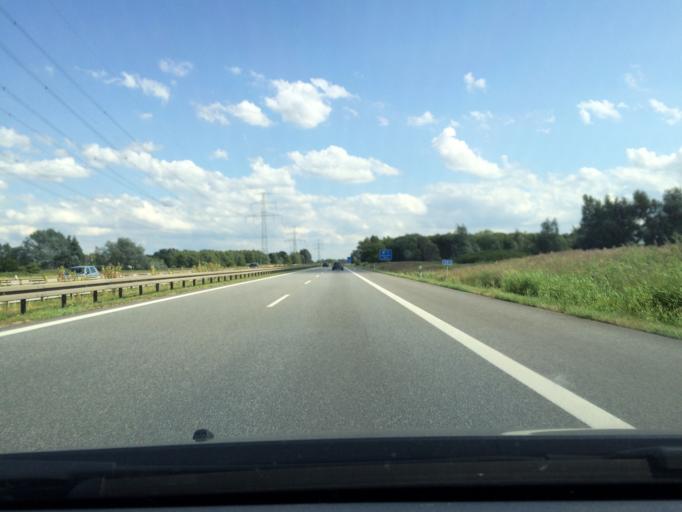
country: DE
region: Mecklenburg-Vorpommern
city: Dierkow-West
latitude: 54.1289
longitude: 12.1484
